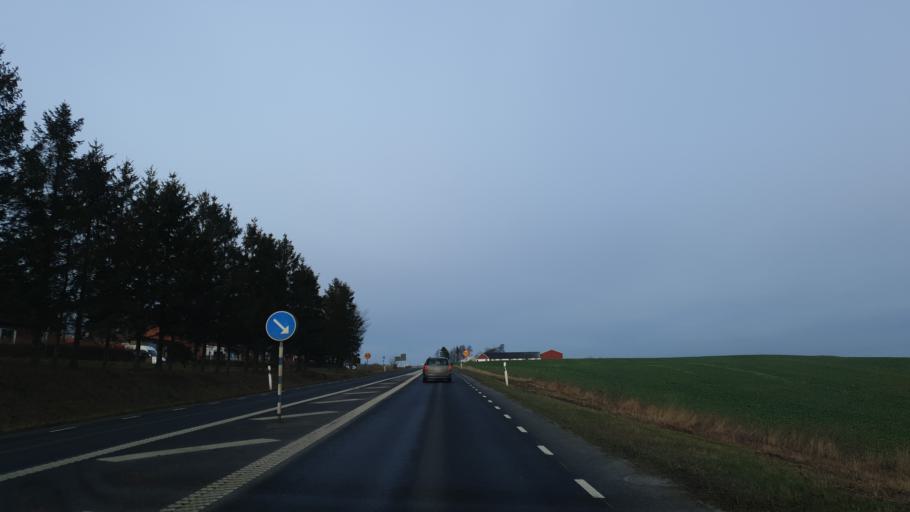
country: SE
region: Skane
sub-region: Ystads Kommun
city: Ystad
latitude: 55.4529
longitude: 13.8008
